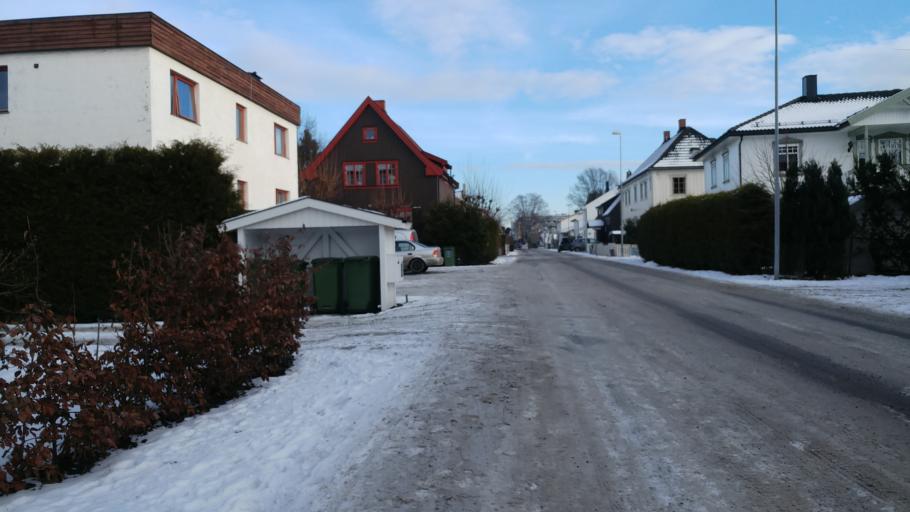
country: NO
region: Akershus
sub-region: Skedsmo
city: Lillestrom
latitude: 59.9572
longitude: 11.0413
